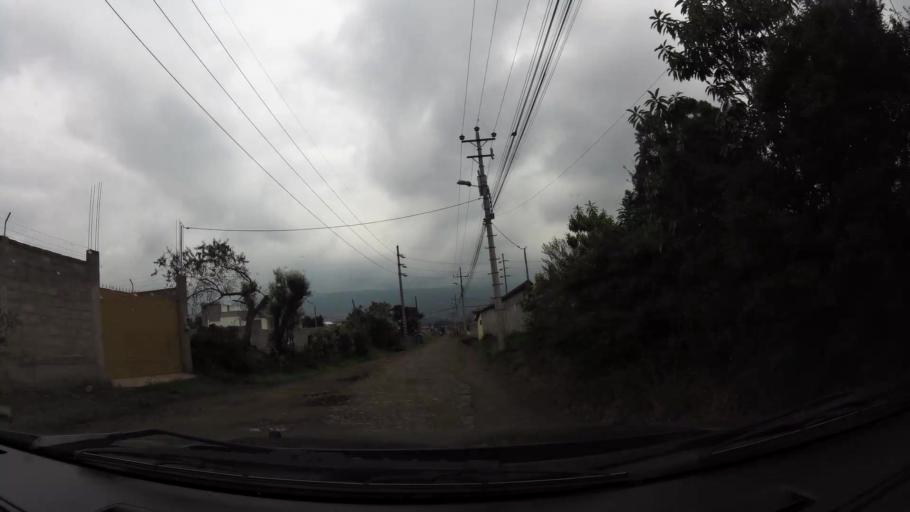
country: EC
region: Pichincha
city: Sangolqui
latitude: -0.3415
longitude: -78.4685
